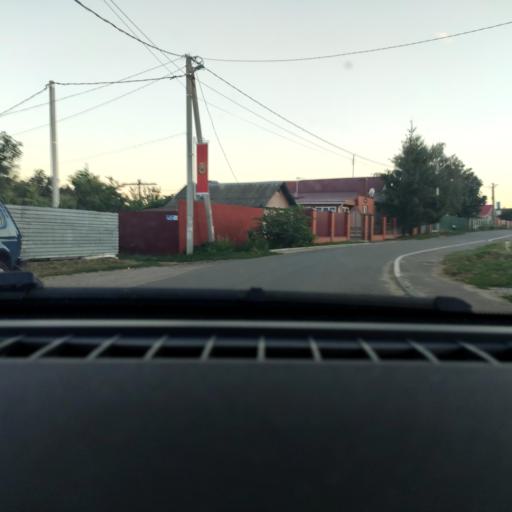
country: RU
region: Voronezj
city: Novaya Usman'
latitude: 51.6567
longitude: 39.3380
